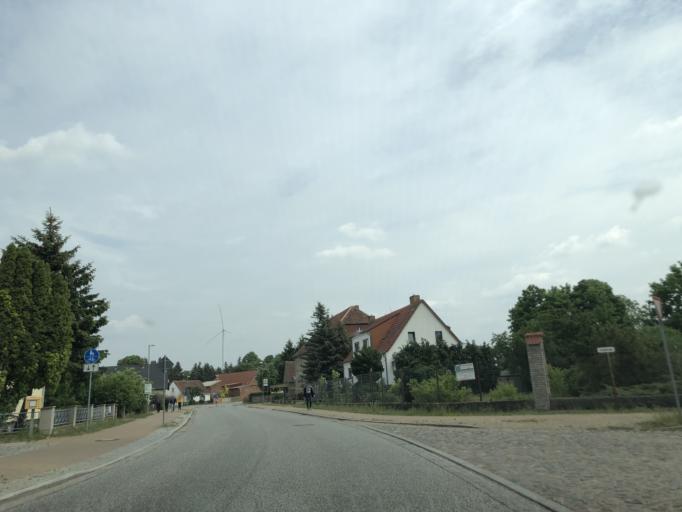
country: DE
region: Brandenburg
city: Gumtow
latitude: 52.9731
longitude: 12.2901
